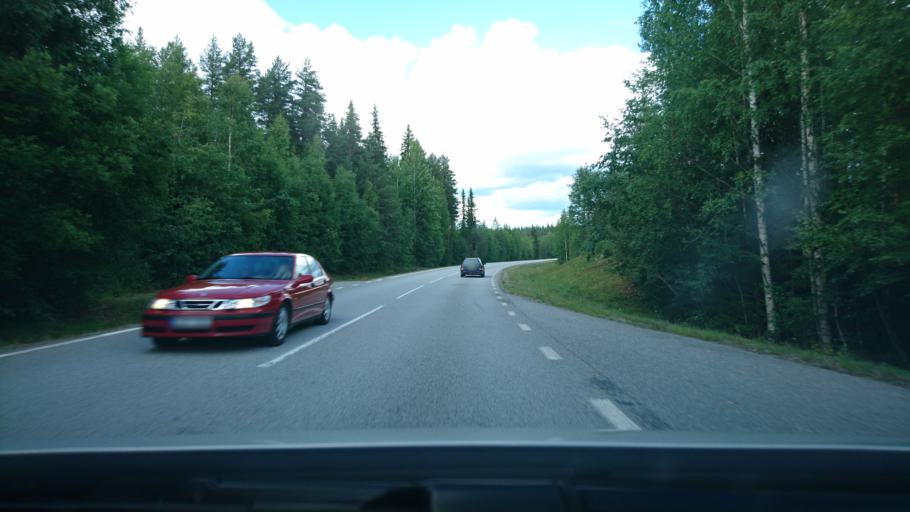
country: SE
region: Vaesternorrland
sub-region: Solleftea Kommun
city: As
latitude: 63.7305
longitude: 16.9848
